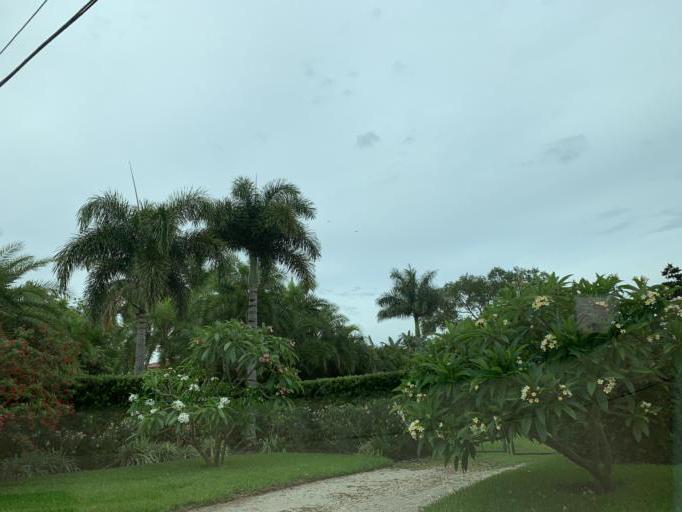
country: US
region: Florida
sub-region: Pinellas County
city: Saint Petersburg
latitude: 27.7915
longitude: -82.6188
